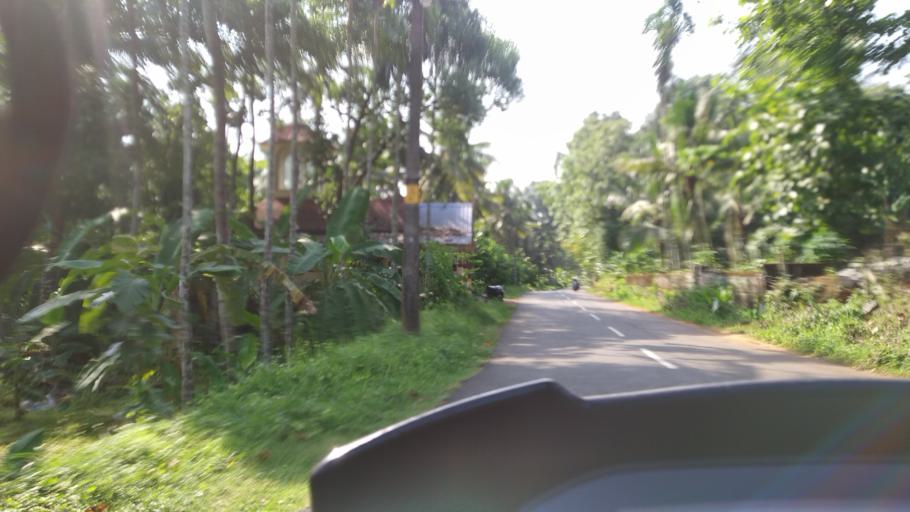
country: IN
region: Kerala
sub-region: Kottayam
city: Palackattumala
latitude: 9.7985
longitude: 76.5870
